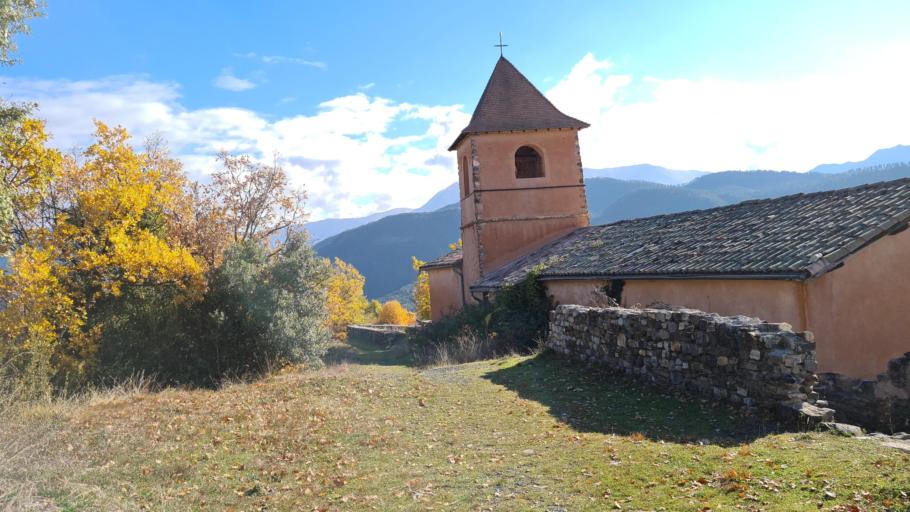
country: FR
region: Provence-Alpes-Cote d'Azur
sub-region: Departement des Alpes-de-Haute-Provence
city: Le Brusquet
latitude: 44.1687
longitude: 6.3098
